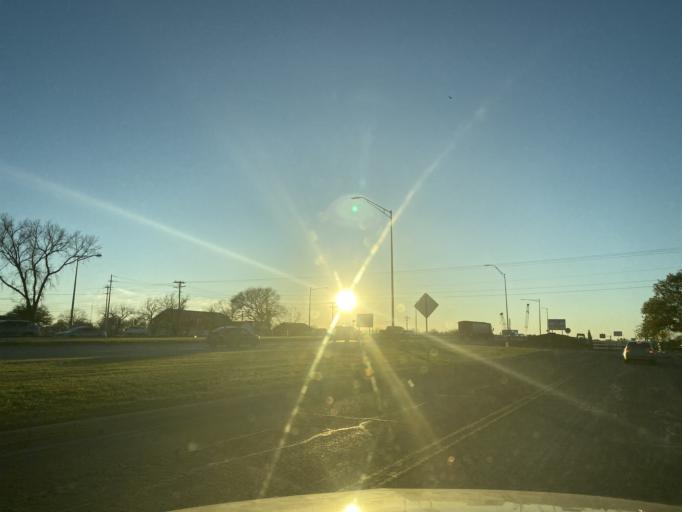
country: US
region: Texas
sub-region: Bastrop County
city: Bastrop
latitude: 30.1053
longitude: -97.3166
